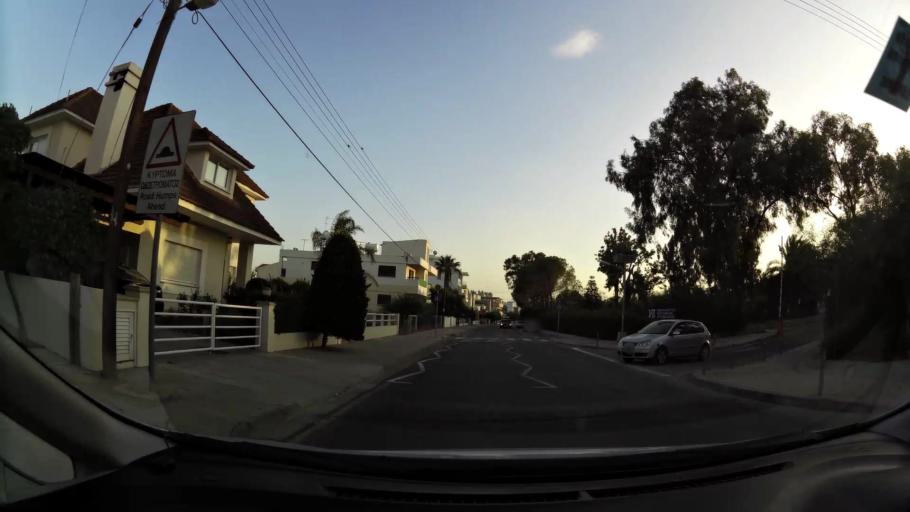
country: CY
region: Lefkosia
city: Nicosia
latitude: 35.1627
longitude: 33.3134
